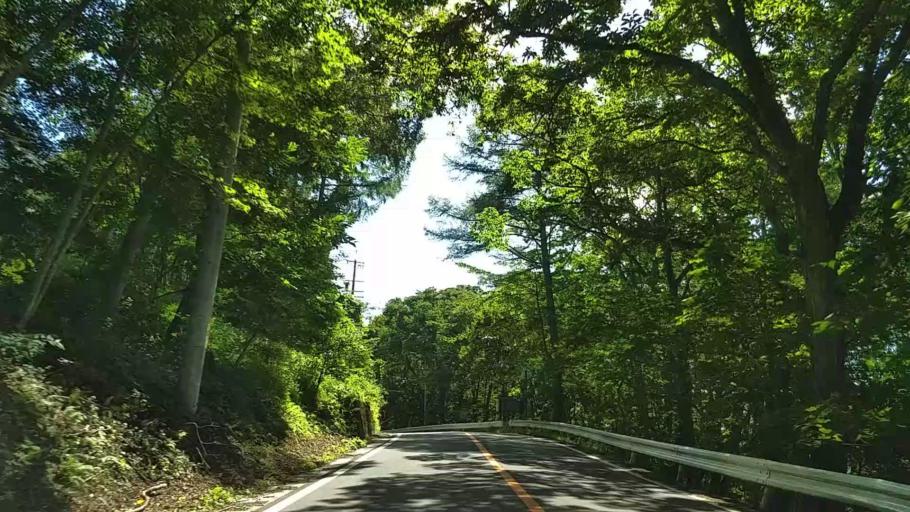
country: JP
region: Nagano
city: Chino
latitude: 36.0552
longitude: 138.2687
